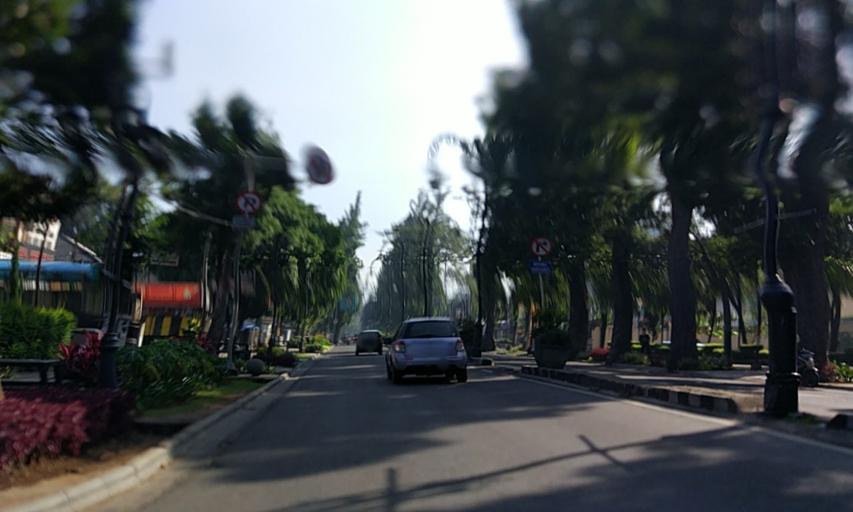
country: ID
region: West Java
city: Bandung
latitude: -6.8937
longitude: 107.6130
